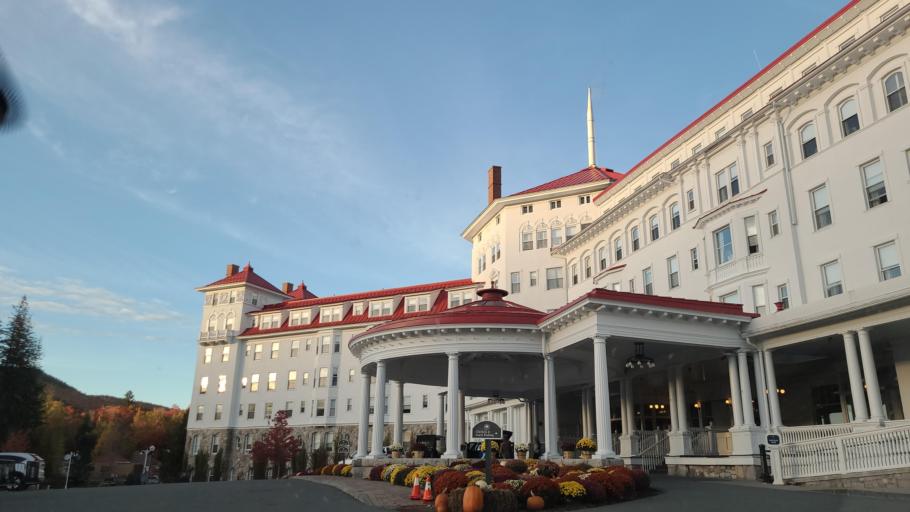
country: US
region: New Hampshire
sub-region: Coos County
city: Jefferson
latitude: 44.2571
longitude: -71.4398
